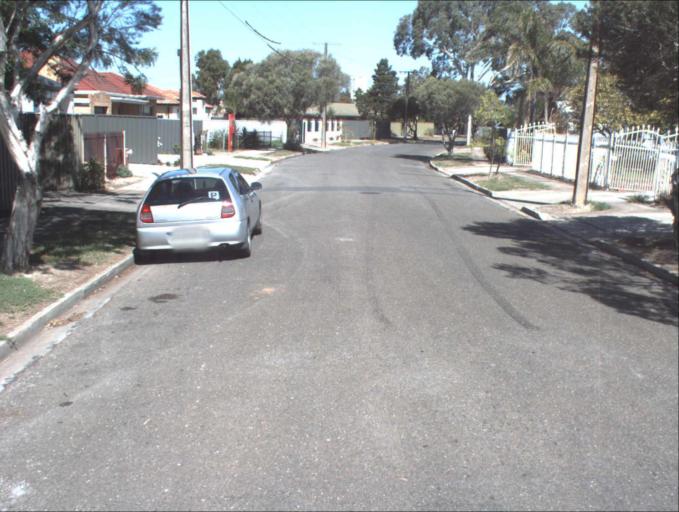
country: AU
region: South Australia
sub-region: Port Adelaide Enfield
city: Enfield
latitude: -34.8381
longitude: 138.5879
